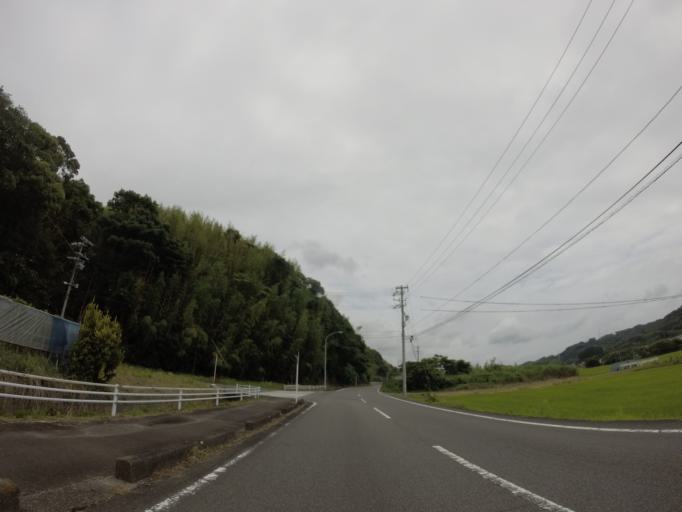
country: JP
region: Shizuoka
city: Shimada
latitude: 34.7781
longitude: 138.1726
